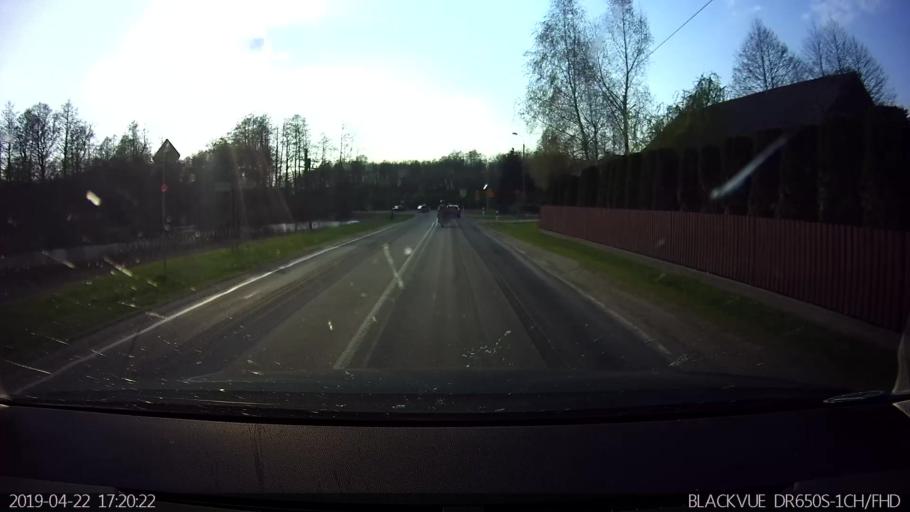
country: PL
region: Masovian Voivodeship
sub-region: Powiat sokolowski
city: Repki
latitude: 52.3885
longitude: 22.3830
